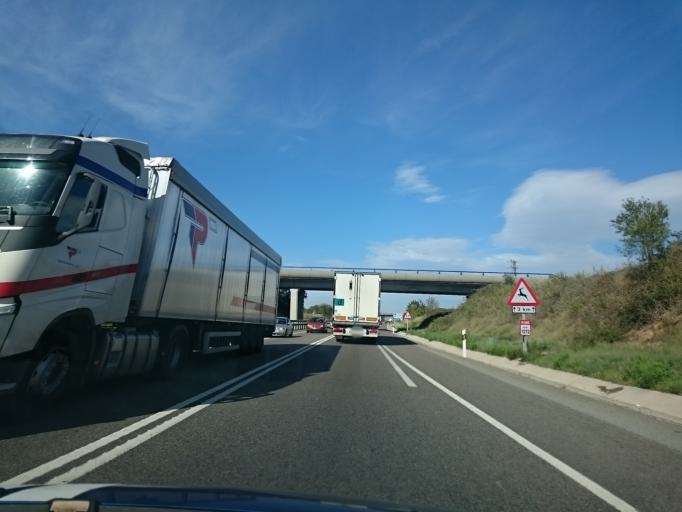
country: ES
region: Catalonia
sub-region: Provincia de Barcelona
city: Vilafranca del Penedes
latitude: 41.3393
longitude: 1.7083
